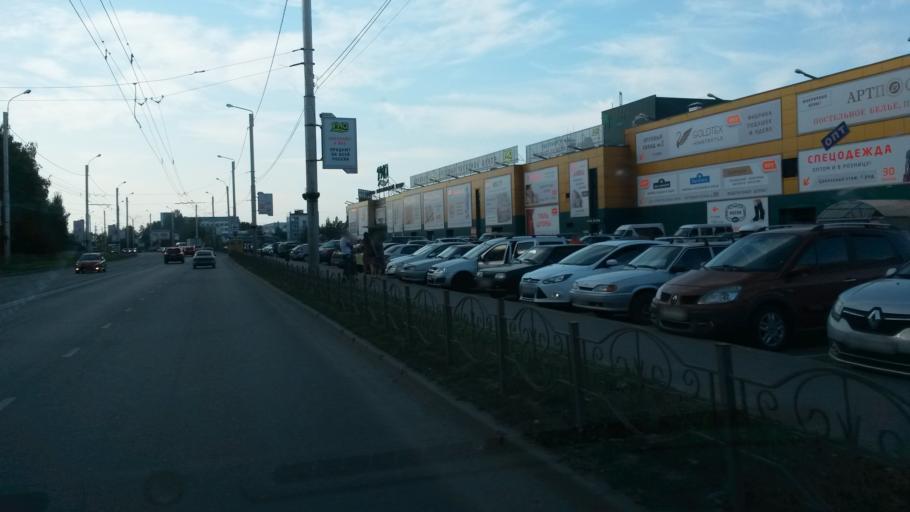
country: RU
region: Ivanovo
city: Kokhma
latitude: 56.9556
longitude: 41.0408
